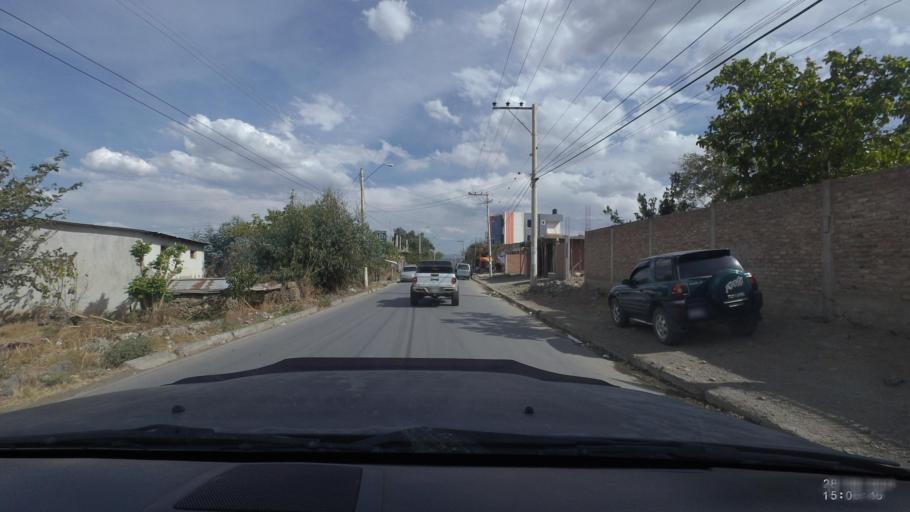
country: BO
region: Cochabamba
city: Cochabamba
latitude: -17.3342
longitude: -66.2835
